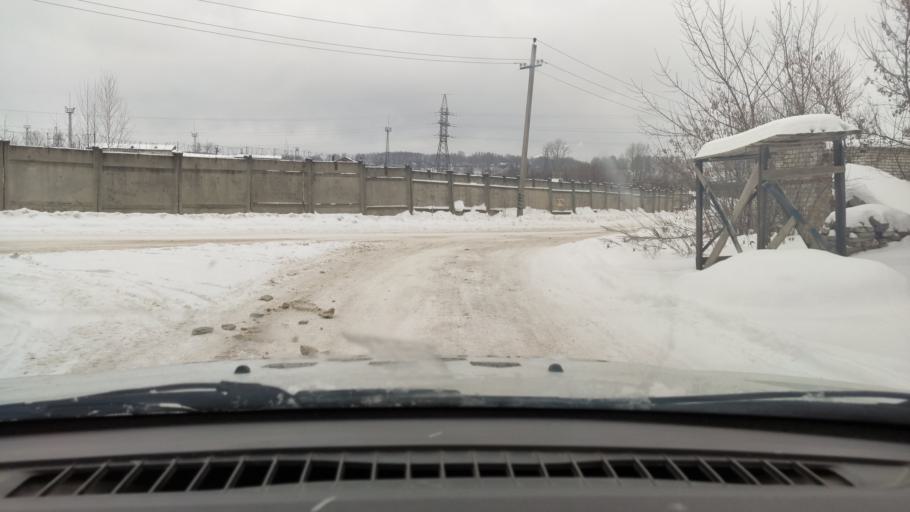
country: RU
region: Perm
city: Kungur
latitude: 57.4485
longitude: 56.9281
